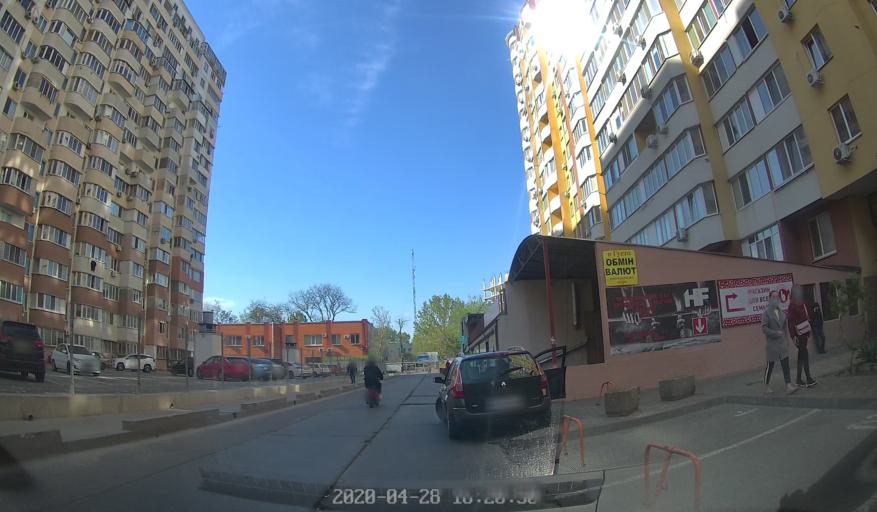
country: NG
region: Niger
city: Lemu
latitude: 9.2808
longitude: 6.1412
